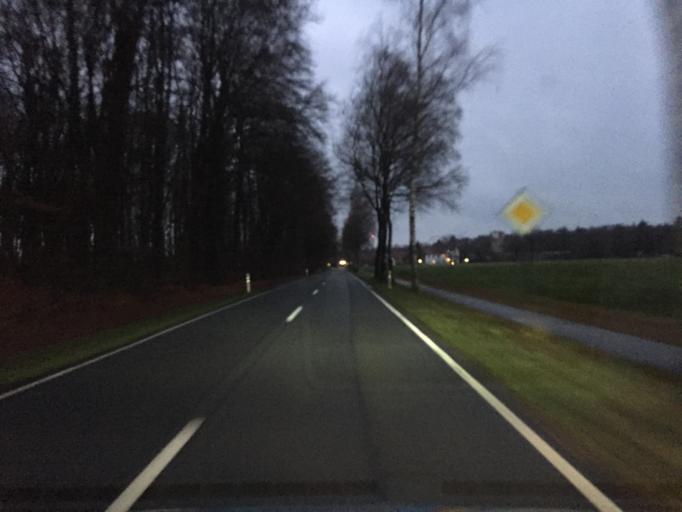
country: DE
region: Lower Saxony
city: Schwaforden
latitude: 52.7450
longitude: 8.8214
